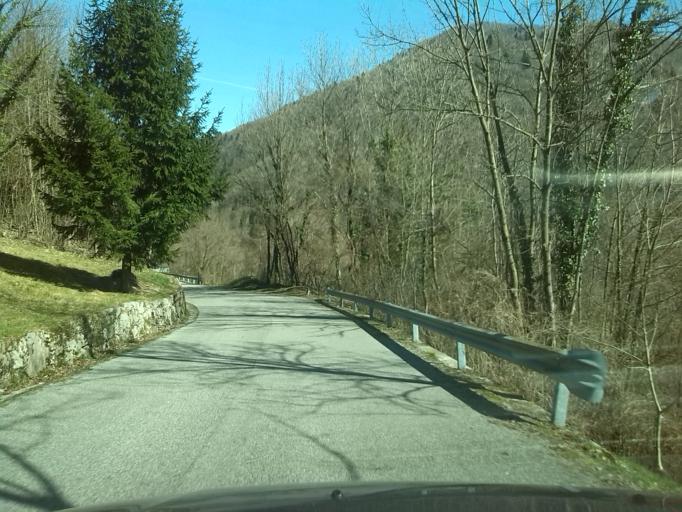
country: IT
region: Friuli Venezia Giulia
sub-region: Provincia di Udine
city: Clodig
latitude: 46.1803
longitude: 13.5751
